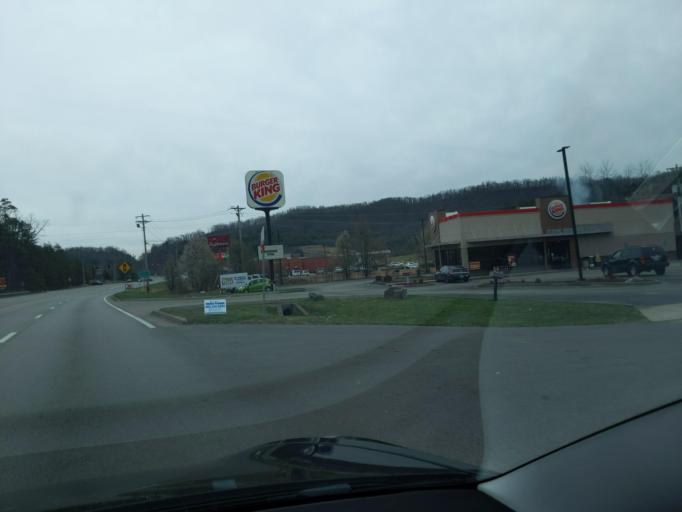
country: US
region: Kentucky
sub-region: Whitley County
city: Corbin
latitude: 36.9184
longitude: -84.1251
